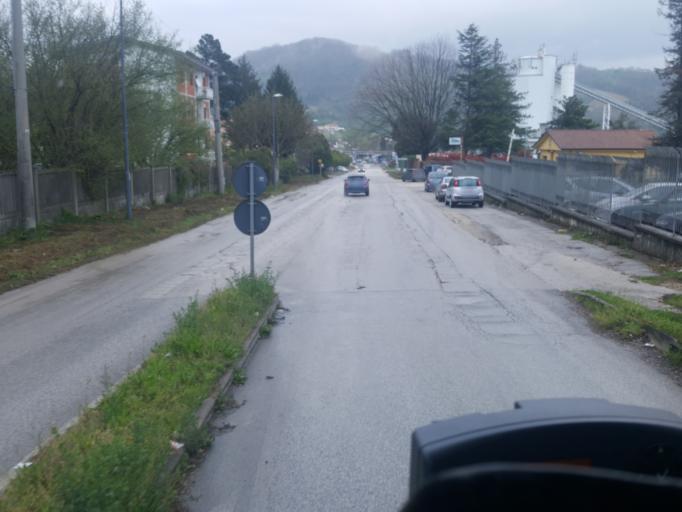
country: IT
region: Campania
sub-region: Provincia di Avellino
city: Atripalda
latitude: 40.9386
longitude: 14.8210
